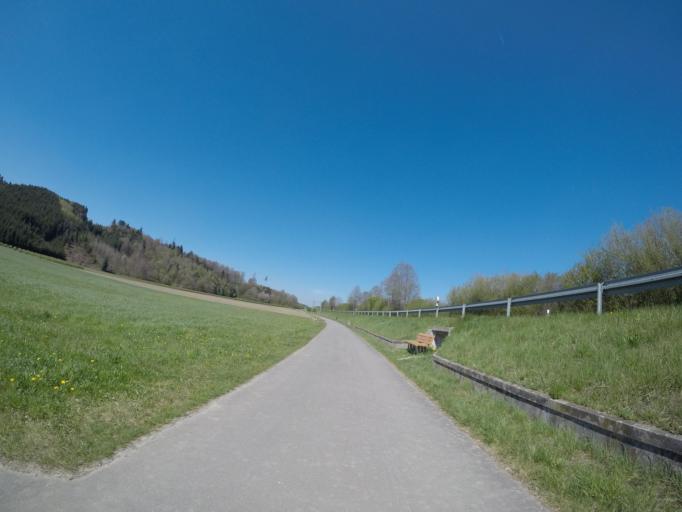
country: DE
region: Baden-Wuerttemberg
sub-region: Tuebingen Region
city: Markdorf
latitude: 47.7717
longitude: 9.4199
